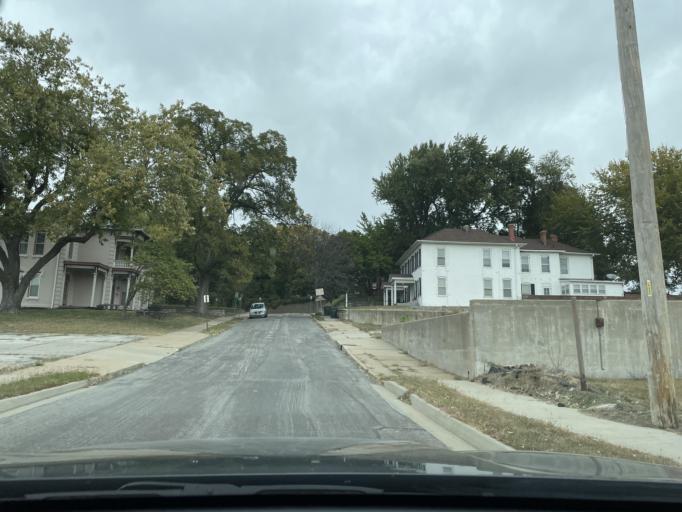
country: US
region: Missouri
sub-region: Buchanan County
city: Saint Joseph
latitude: 39.7702
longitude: -94.8506
